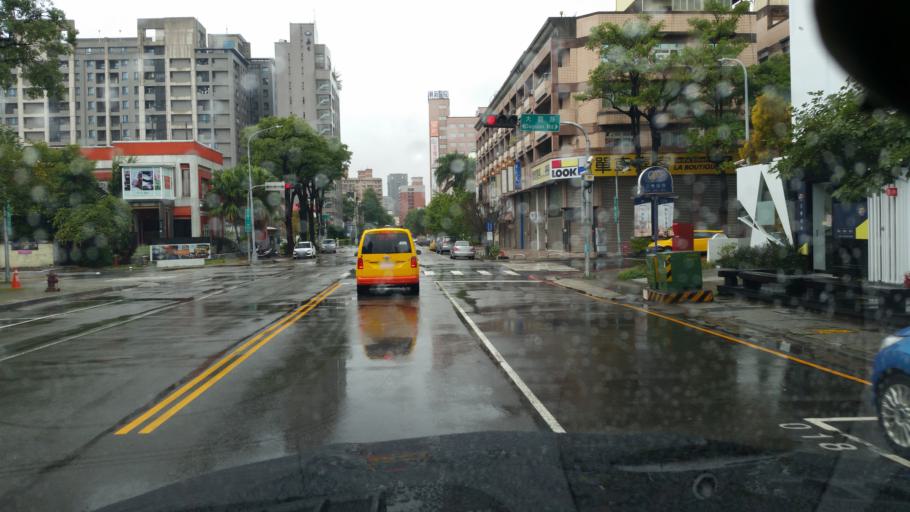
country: TW
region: Taiwan
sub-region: Taichung City
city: Taichung
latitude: 24.1488
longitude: 120.6430
